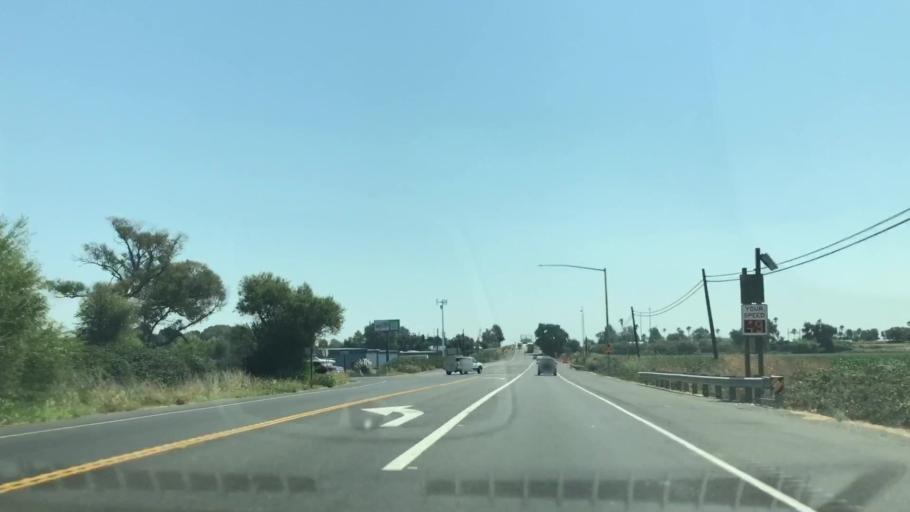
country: US
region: California
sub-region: Solano County
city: Rio Vista
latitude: 38.1289
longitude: -121.5869
